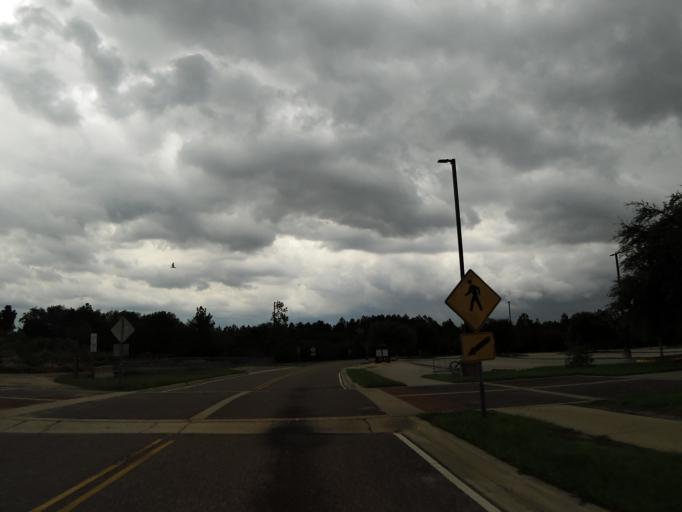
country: US
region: Florida
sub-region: Duval County
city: Jacksonville Beach
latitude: 30.2784
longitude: -81.5117
